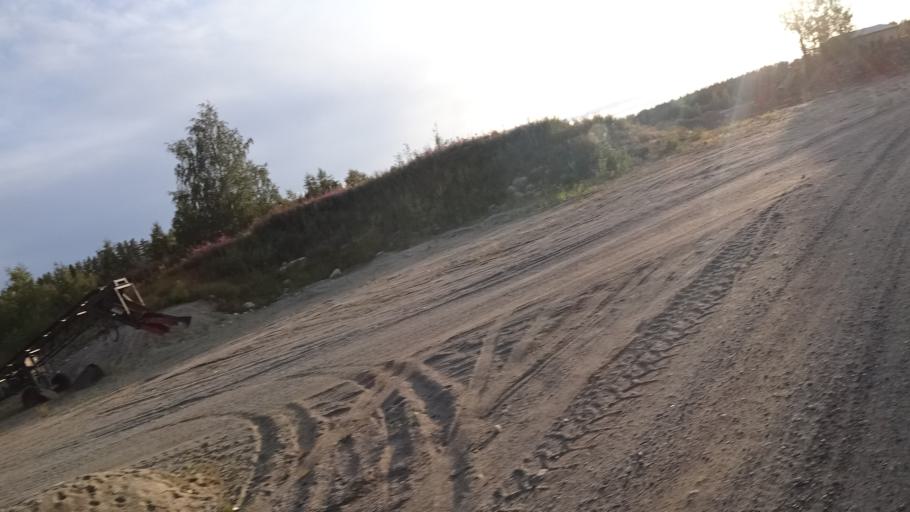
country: FI
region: North Karelia
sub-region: Joensuu
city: Ilomantsi
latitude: 62.6396
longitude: 31.0737
